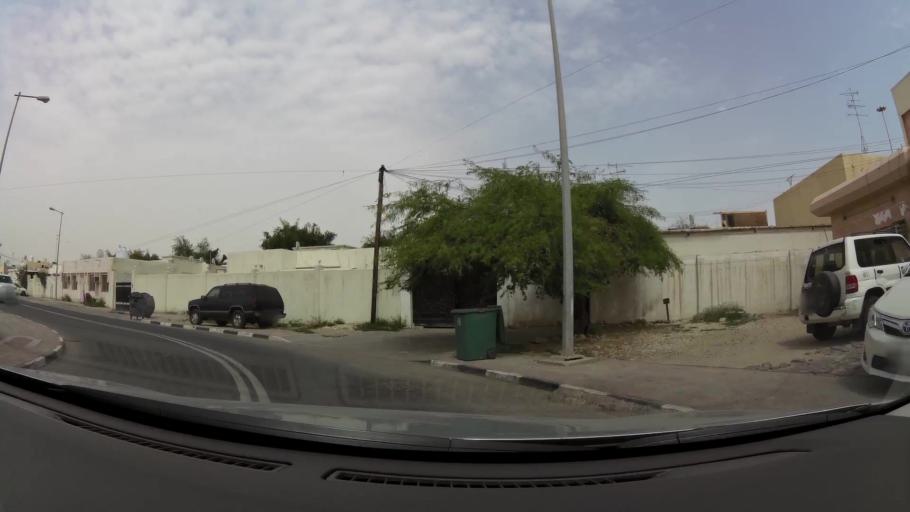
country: QA
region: Baladiyat ad Dawhah
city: Doha
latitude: 25.3142
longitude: 51.4865
